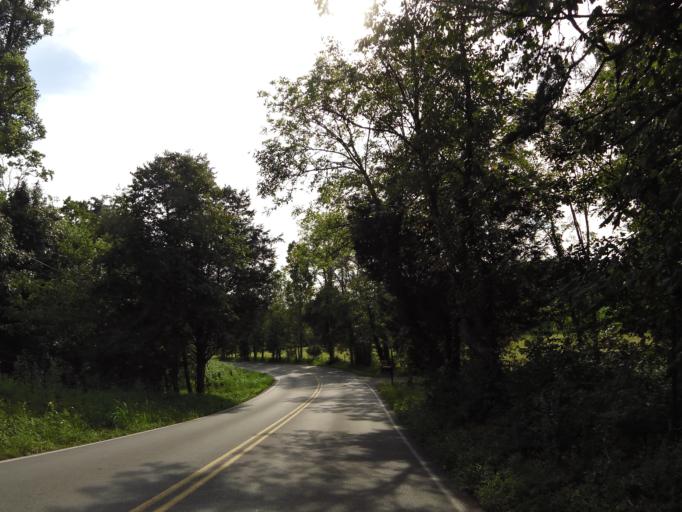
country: US
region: Tennessee
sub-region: Sevier County
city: Seymour
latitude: 35.8766
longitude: -83.7833
